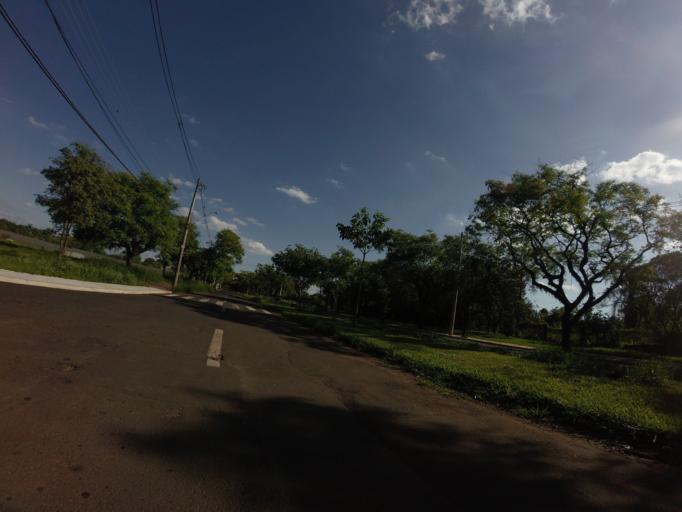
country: BR
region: Sao Paulo
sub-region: Piracicaba
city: Piracicaba
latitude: -22.7584
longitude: -47.5937
